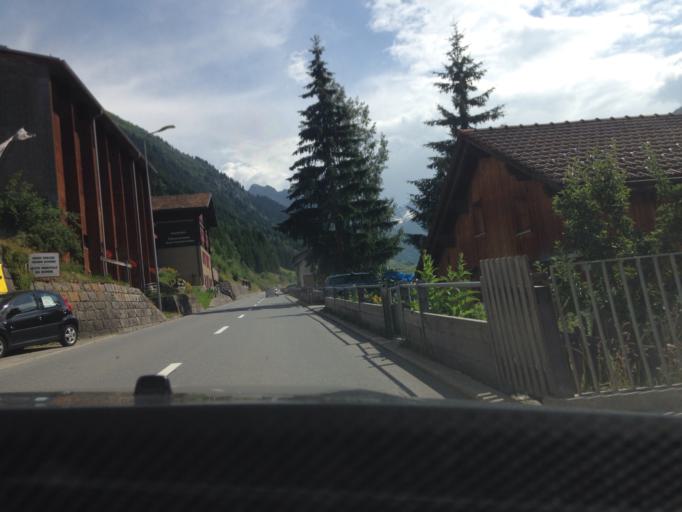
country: CH
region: Grisons
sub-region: Surselva District
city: Disentis
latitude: 46.6721
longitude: 8.8587
